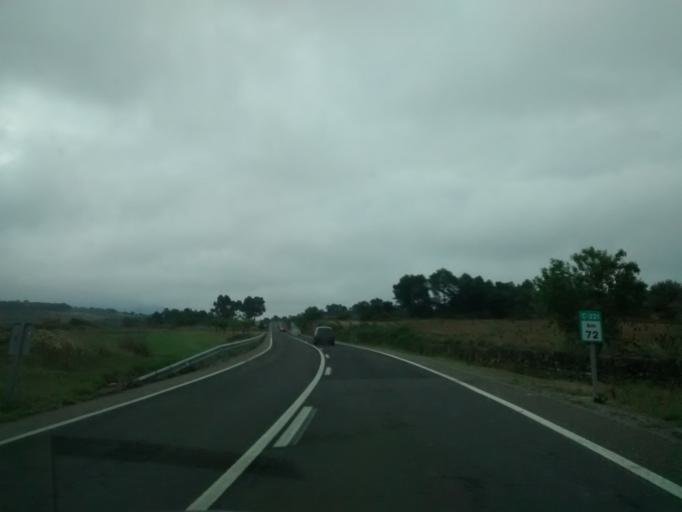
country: ES
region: Catalonia
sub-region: Provincia de Tarragona
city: Bot
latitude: 41.0550
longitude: 0.3608
